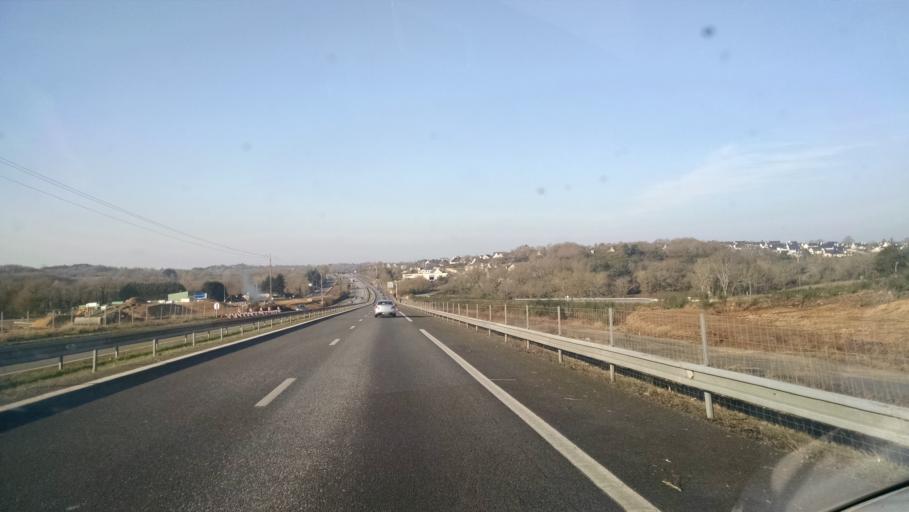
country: FR
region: Brittany
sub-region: Departement du Morbihan
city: Muzillac
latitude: 47.5494
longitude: -2.4631
